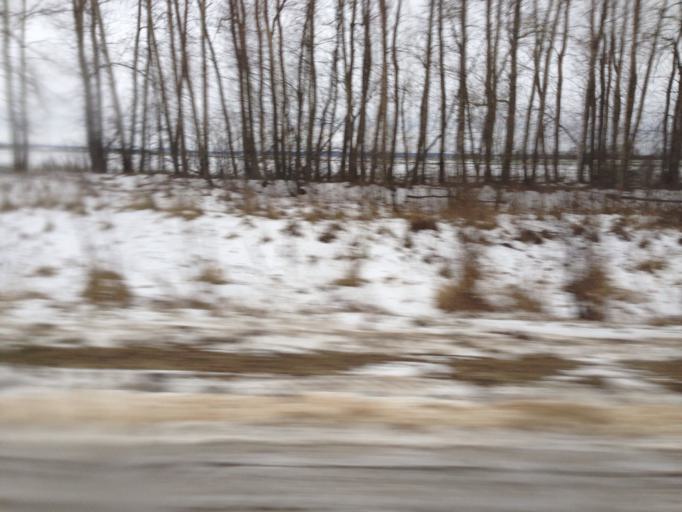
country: RU
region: Tula
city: Bolokhovo
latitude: 54.0778
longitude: 37.7850
